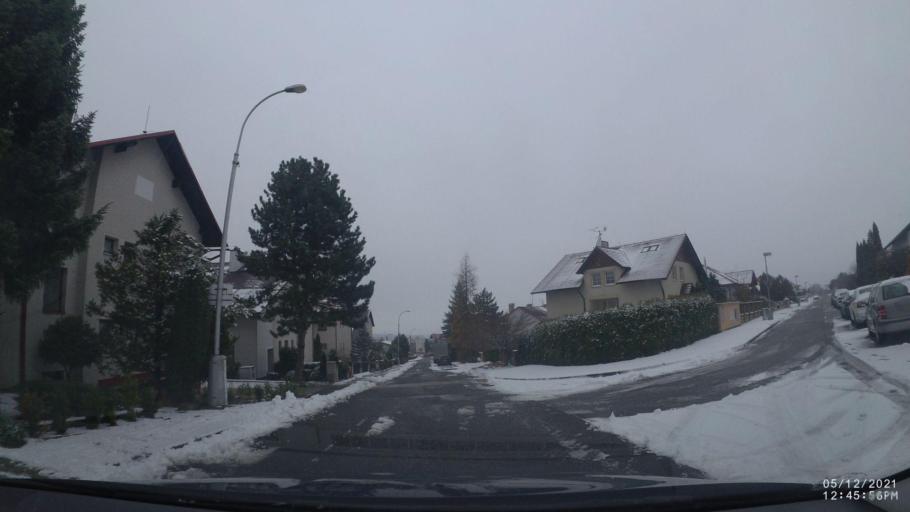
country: CZ
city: Nove Mesto nad Metuji
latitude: 50.3590
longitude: 16.1569
